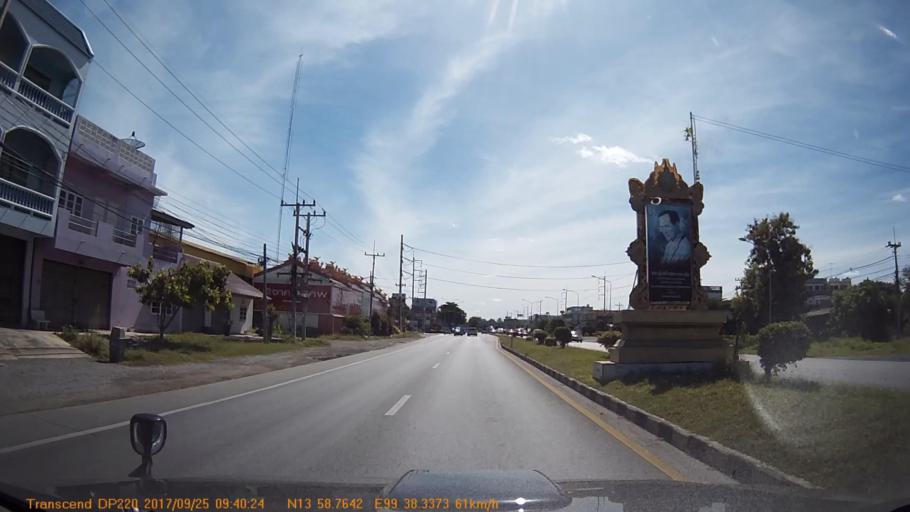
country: TH
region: Kanchanaburi
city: Tha Muang
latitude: 13.9794
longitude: 99.6390
